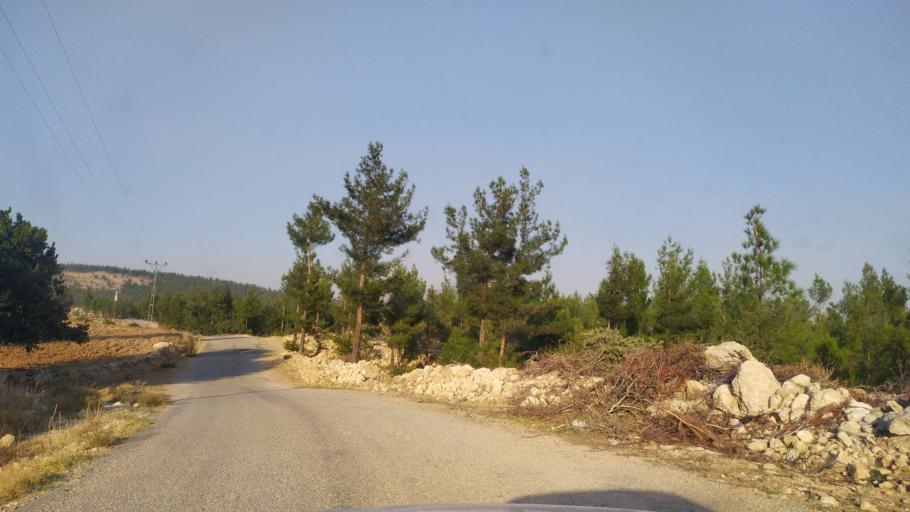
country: TR
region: Mersin
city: Mut
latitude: 36.6866
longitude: 33.1956
